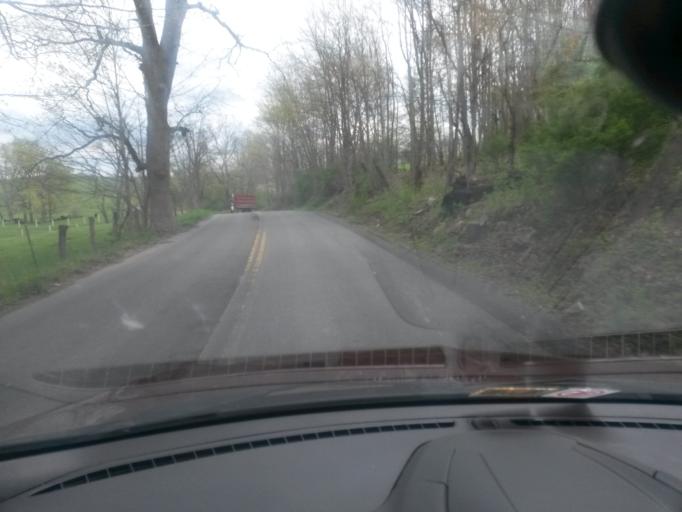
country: US
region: West Virginia
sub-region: Greenbrier County
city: Lewisburg
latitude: 37.8916
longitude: -80.4255
